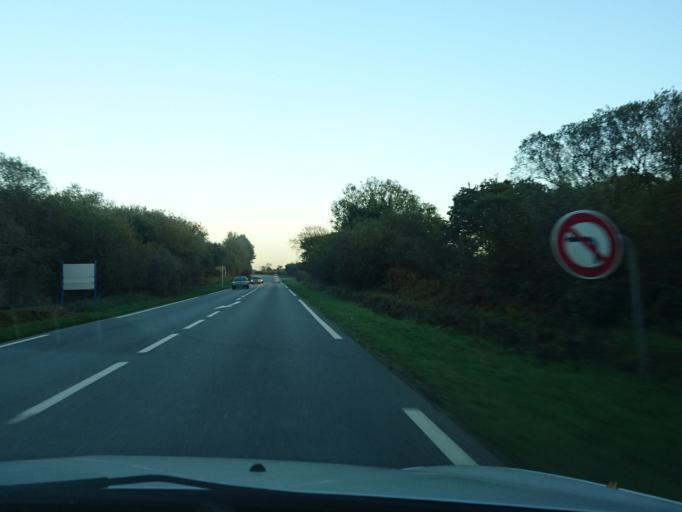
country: FR
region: Brittany
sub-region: Departement du Finistere
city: Saint-Renan
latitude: 48.4325
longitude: -4.6120
